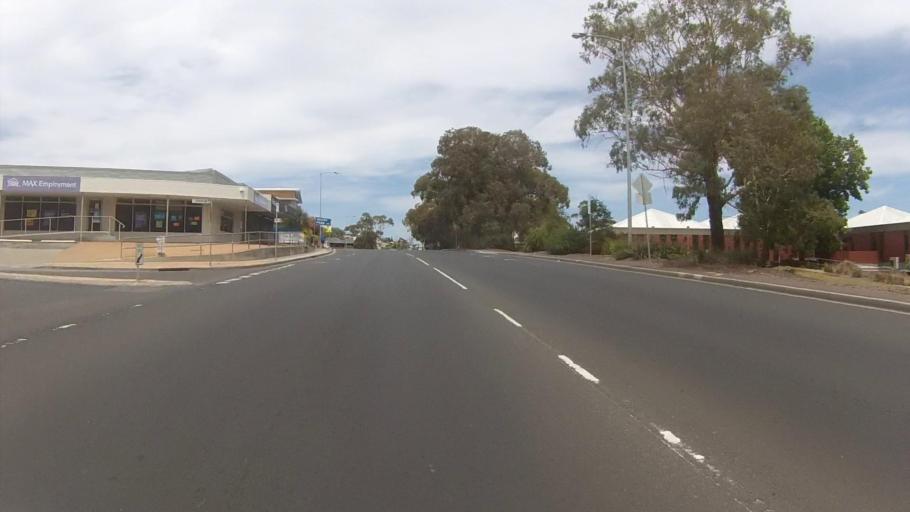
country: AU
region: Tasmania
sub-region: Clarence
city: Warrane
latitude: -42.8620
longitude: 147.3712
